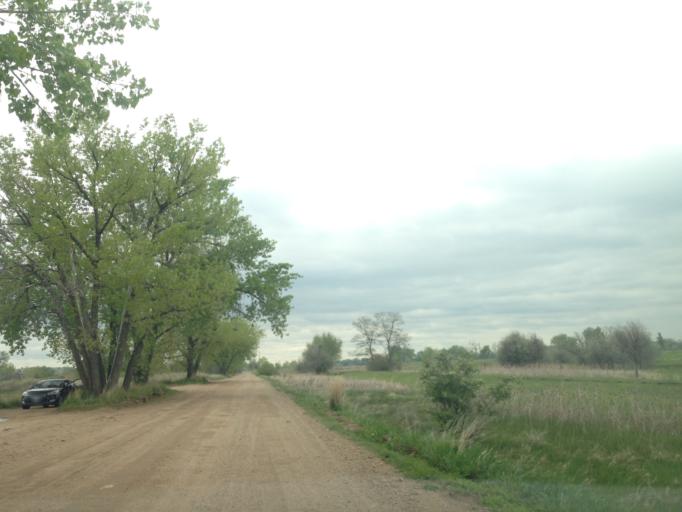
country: US
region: Colorado
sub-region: Boulder County
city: Gunbarrel
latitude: 40.0395
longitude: -105.1846
